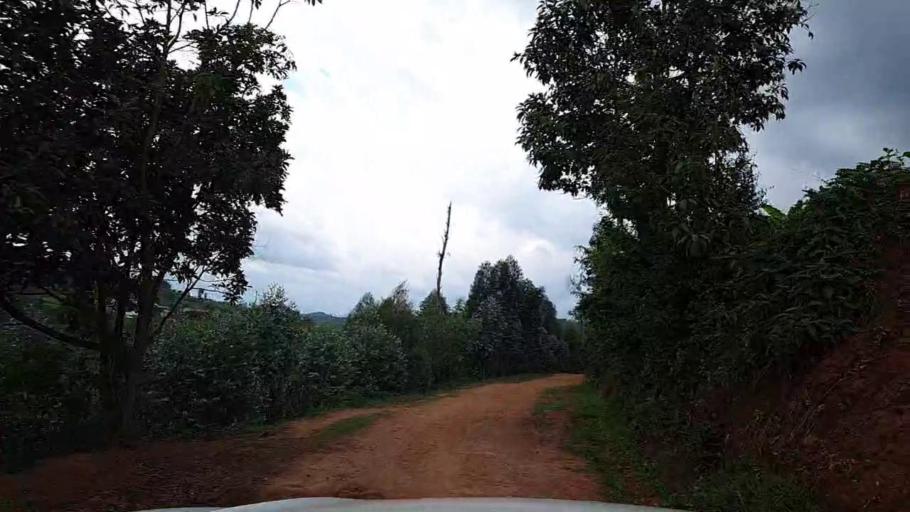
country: RW
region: Southern Province
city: Gikongoro
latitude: -2.4161
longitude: 29.6595
